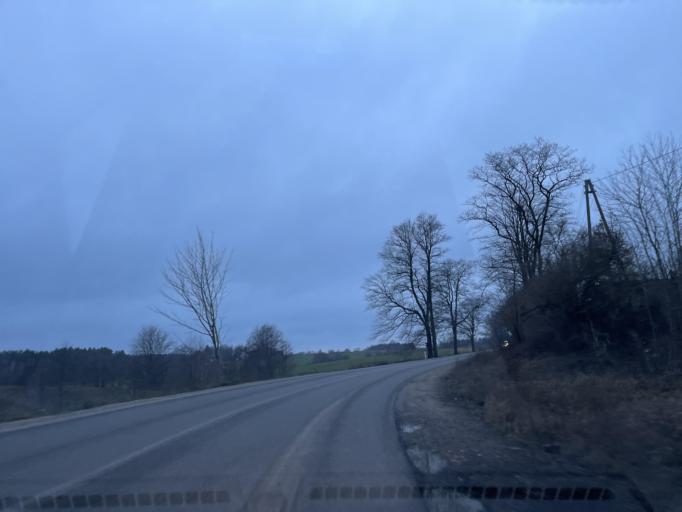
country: PL
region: Pomeranian Voivodeship
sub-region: Powiat wejherowski
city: Szemud
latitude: 54.4161
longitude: 18.1934
